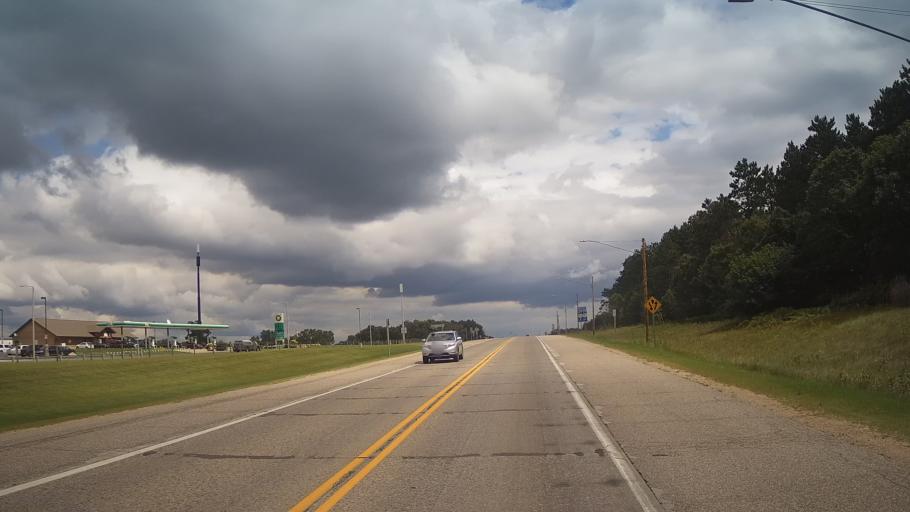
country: US
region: Wisconsin
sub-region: Marquette County
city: Westfield
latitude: 44.0343
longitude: -89.5353
